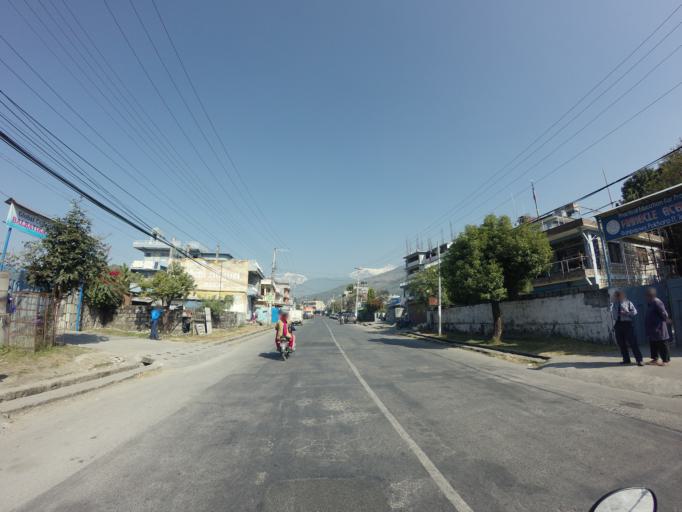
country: NP
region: Western Region
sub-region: Gandaki Zone
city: Pokhara
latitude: 28.2184
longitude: 83.9976
